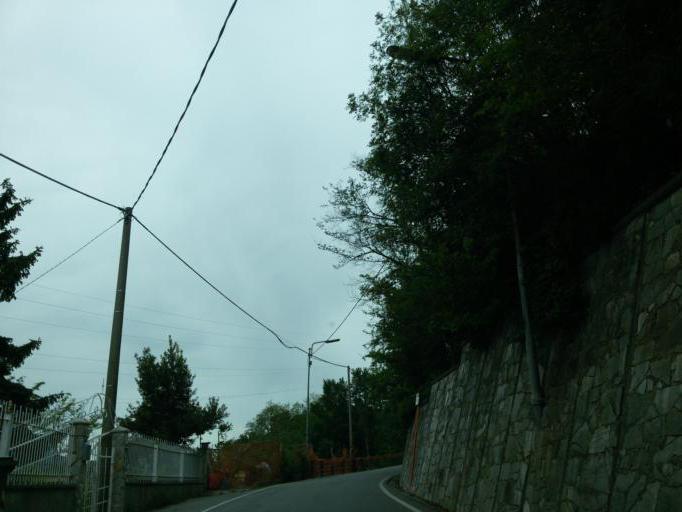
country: IT
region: Liguria
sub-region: Provincia di Genova
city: Genoa
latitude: 44.4330
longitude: 8.9128
